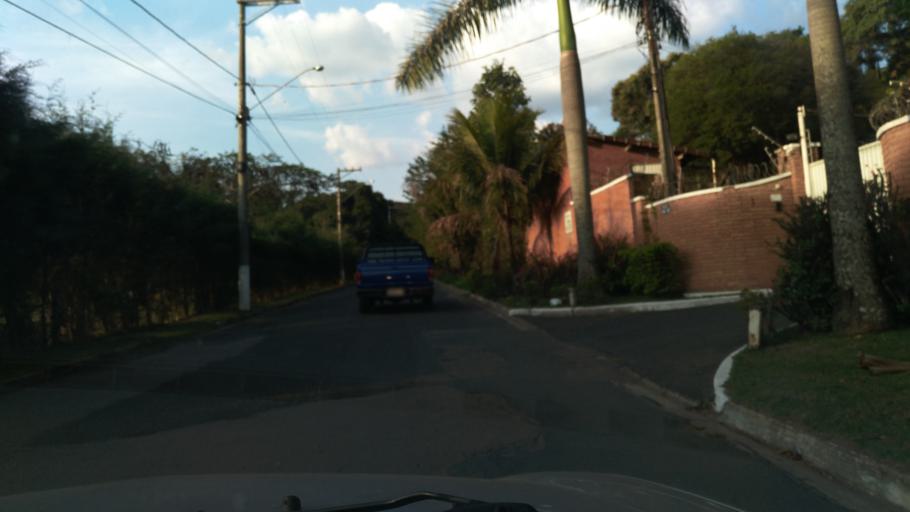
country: BR
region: Sao Paulo
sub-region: Vinhedo
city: Vinhedo
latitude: -23.0313
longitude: -47.0078
